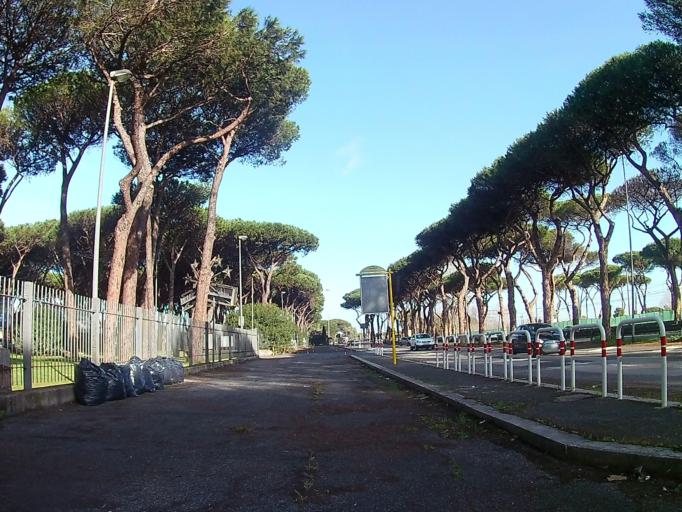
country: IT
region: Latium
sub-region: Citta metropolitana di Roma Capitale
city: Lido di Ostia
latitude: 41.7457
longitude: 12.2878
